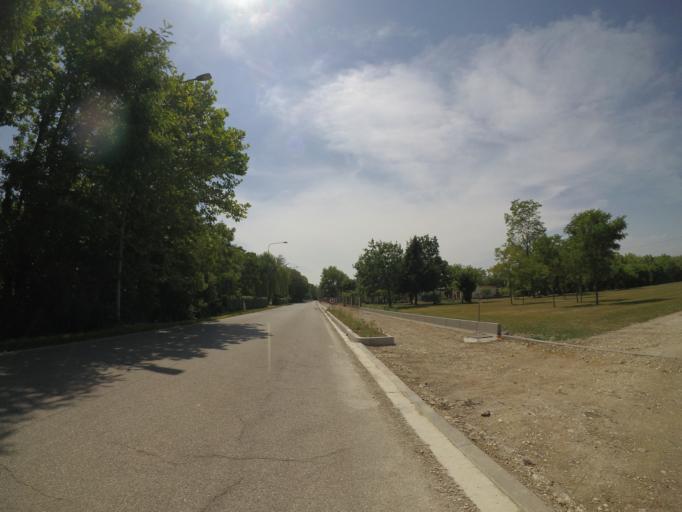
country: IT
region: Friuli Venezia Giulia
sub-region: Provincia di Udine
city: Codroipo
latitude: 45.9604
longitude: 12.9661
